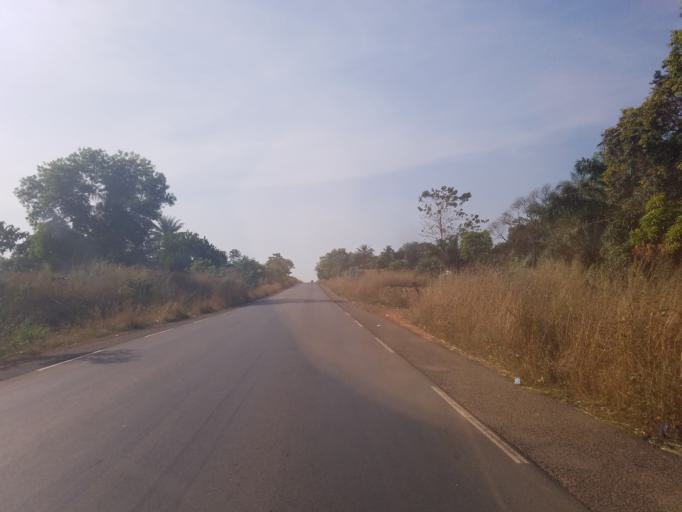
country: GN
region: Boke
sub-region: Boffa
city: Boffa
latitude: 10.1886
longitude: -14.0476
